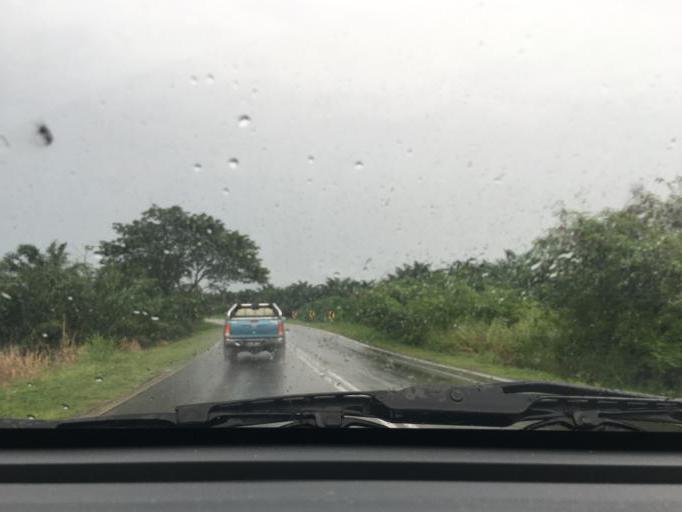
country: MY
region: Kedah
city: Sungai Petani
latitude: 5.6029
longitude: 100.6403
